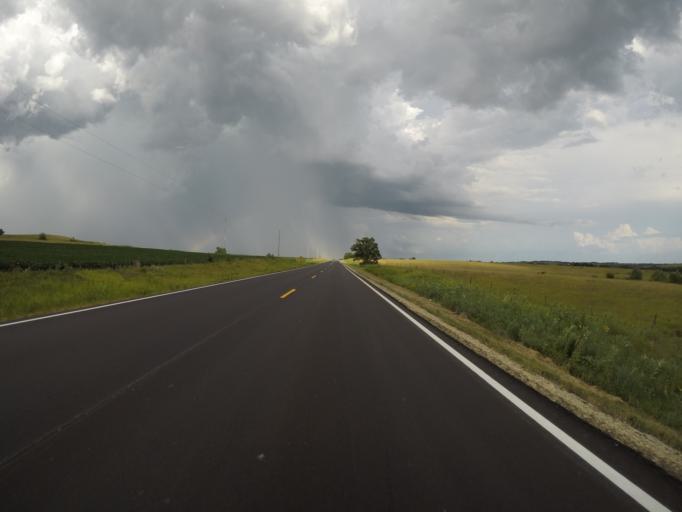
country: US
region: Kansas
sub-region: Marshall County
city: Blue Rapids
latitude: 39.4365
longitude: -96.8059
